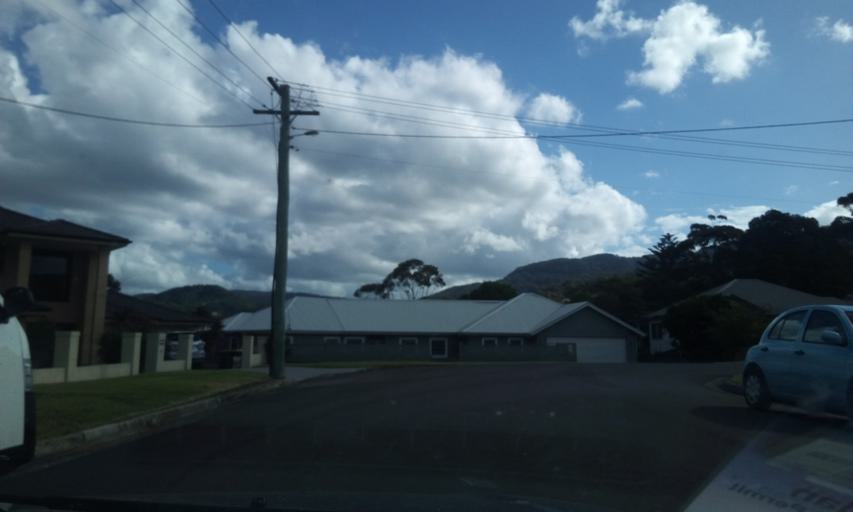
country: AU
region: New South Wales
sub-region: Wollongong
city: Keiraville
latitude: -34.4145
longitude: 150.8661
